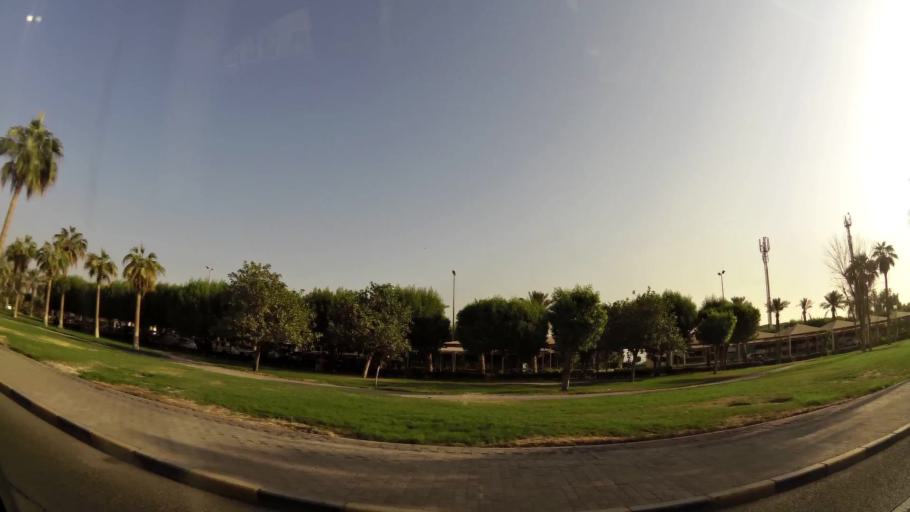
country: KW
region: Muhafazat Hawalli
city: Hawalli
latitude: 29.3428
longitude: 48.0472
